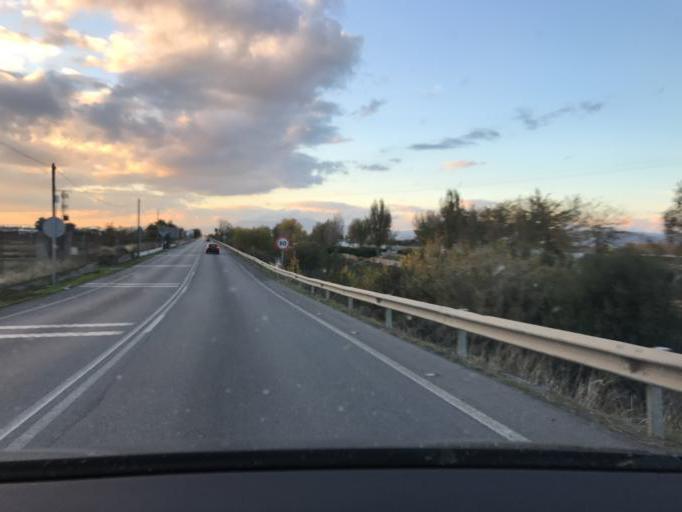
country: ES
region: Andalusia
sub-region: Provincia de Granada
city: Armilla
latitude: 37.1634
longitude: -3.6285
